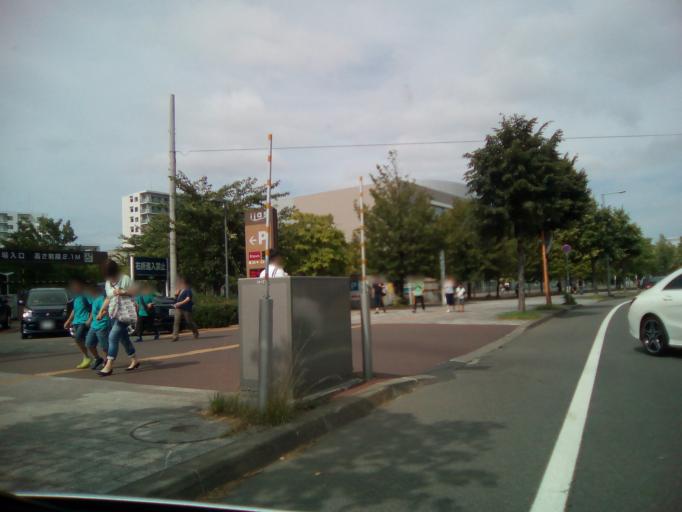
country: JP
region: Hokkaido
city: Sapporo
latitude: 43.0553
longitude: 141.3855
